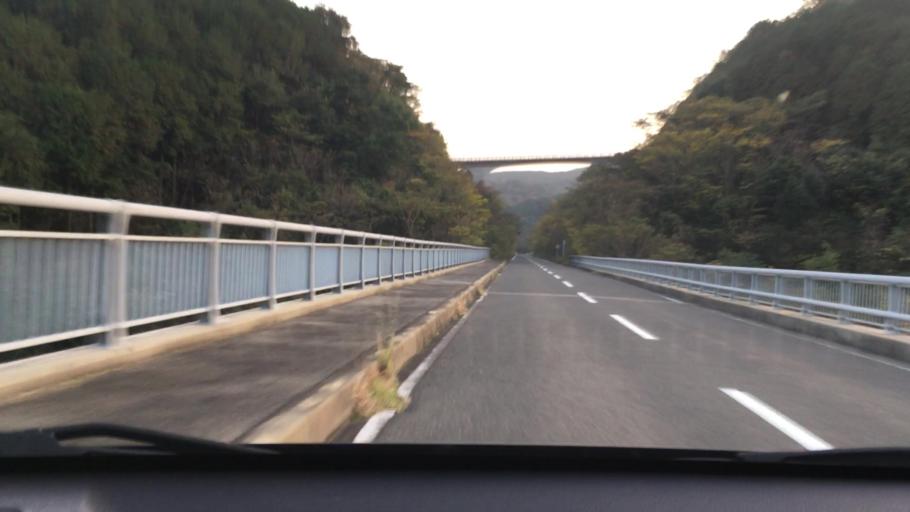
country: JP
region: Nagasaki
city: Sasebo
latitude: 33.0056
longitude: 129.7075
